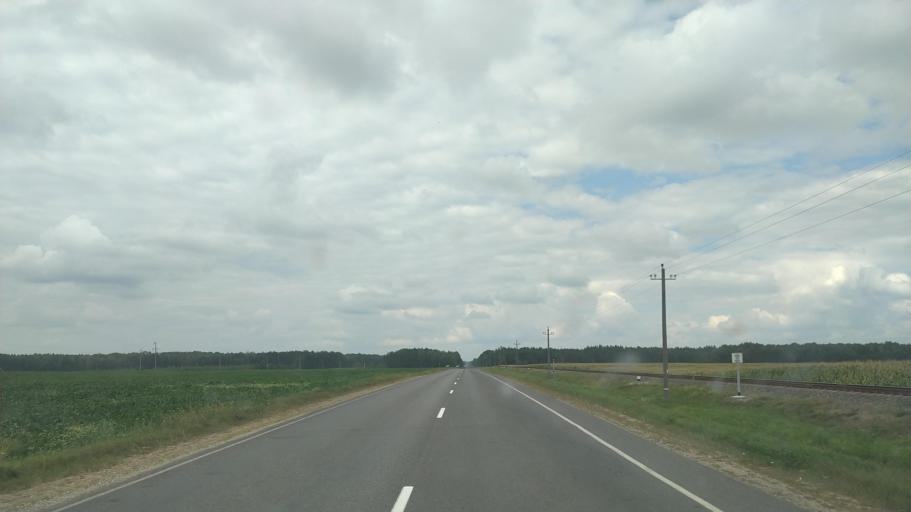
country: BY
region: Brest
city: Byelaazyorsk
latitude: 52.5156
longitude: 25.1537
